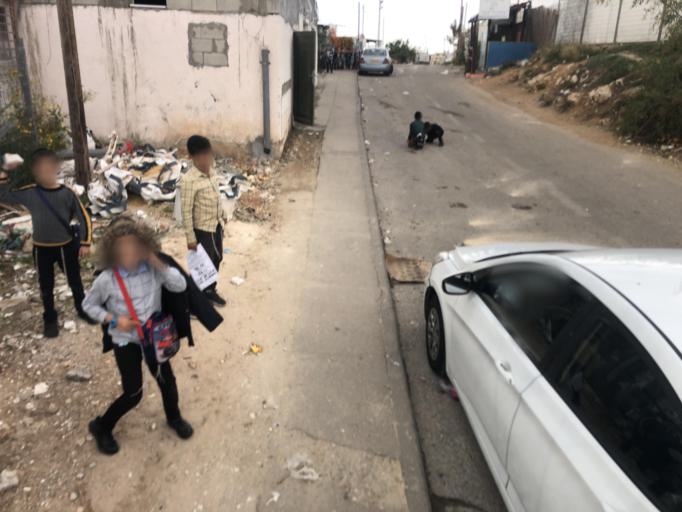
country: IL
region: Jerusalem
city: Modiin Ilit
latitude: 31.9401
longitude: 35.0379
